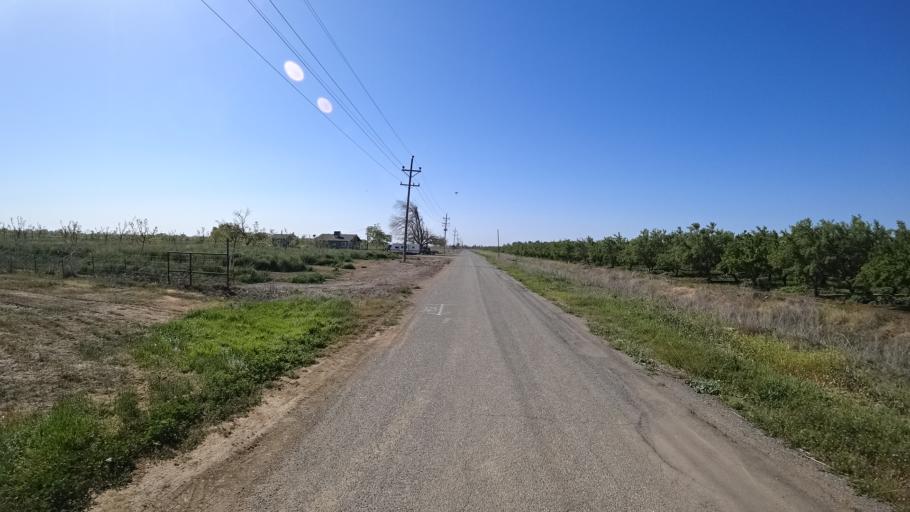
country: US
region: California
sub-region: Glenn County
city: Willows
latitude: 39.5459
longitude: -122.1861
